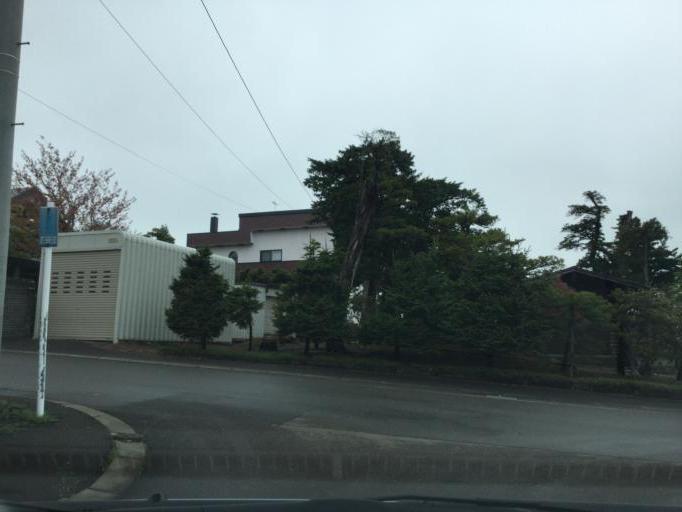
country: JP
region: Hokkaido
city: Iwamizawa
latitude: 43.2179
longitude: 141.7875
